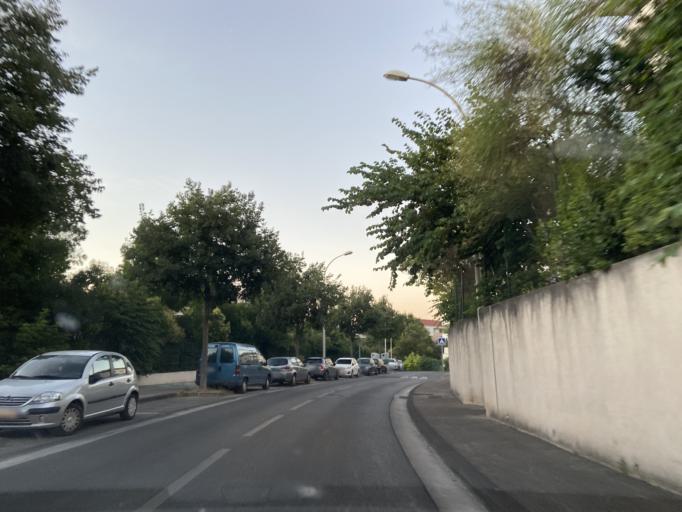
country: FR
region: Provence-Alpes-Cote d'Azur
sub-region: Departement des Bouches-du-Rhone
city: Plan-de-Cuques
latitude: 43.3324
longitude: 5.4513
